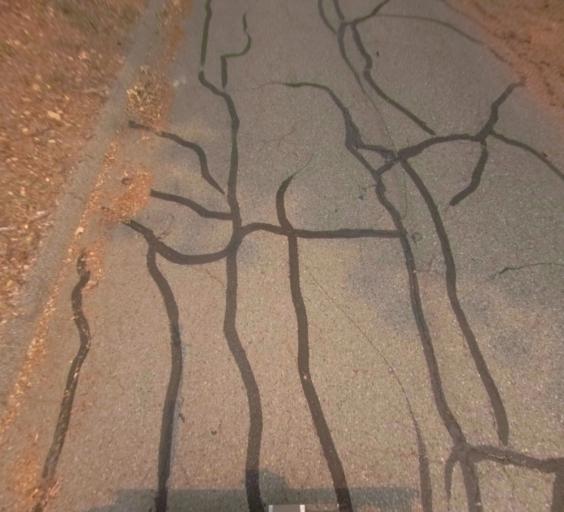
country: US
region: California
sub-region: Madera County
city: Oakhurst
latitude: 37.2681
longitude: -119.5113
